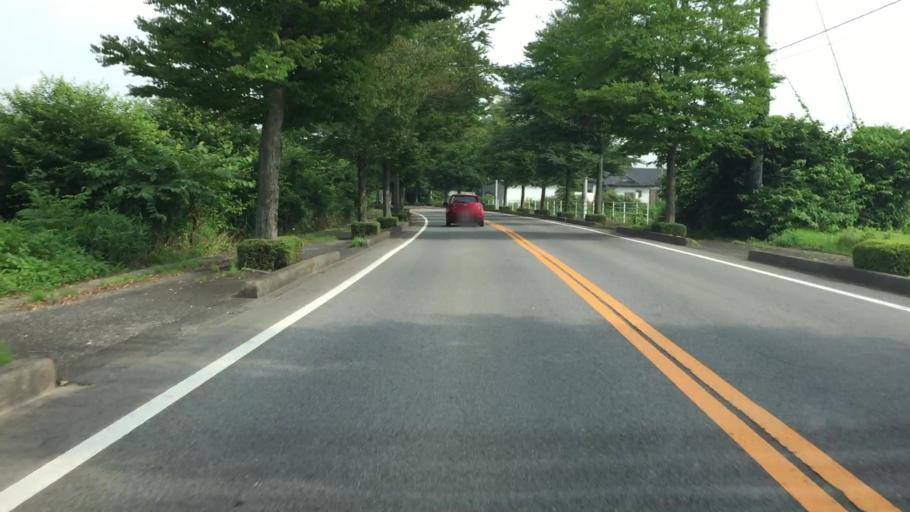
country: JP
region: Tochigi
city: Kuroiso
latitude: 36.9738
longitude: 139.9708
